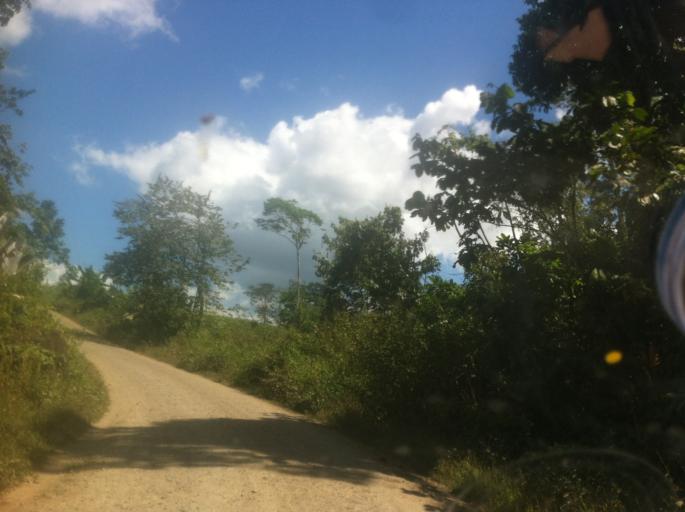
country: CR
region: Alajuela
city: Los Chiles
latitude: 11.2338
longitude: -84.4889
